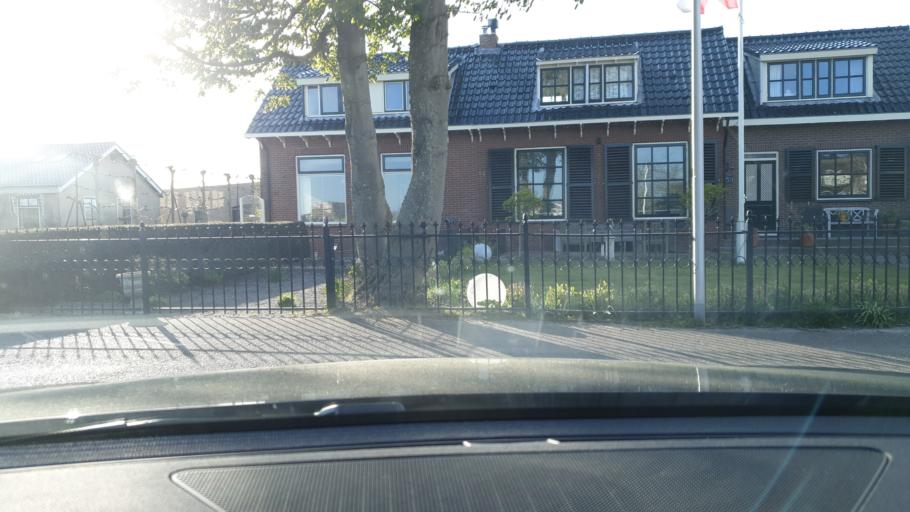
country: NL
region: South Holland
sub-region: Gemeente Teylingen
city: Sassenheim
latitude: 52.2443
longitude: 4.5242
